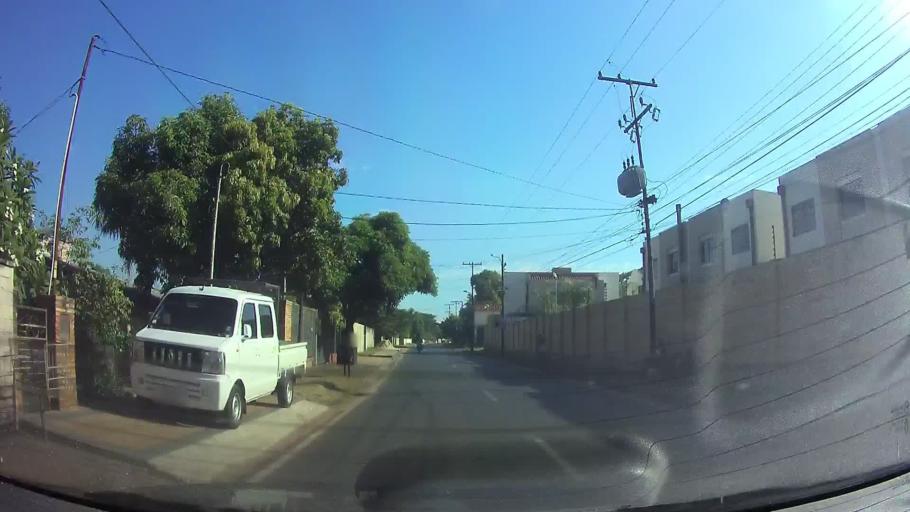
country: PY
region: Central
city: Fernando de la Mora
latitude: -25.2689
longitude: -57.5170
